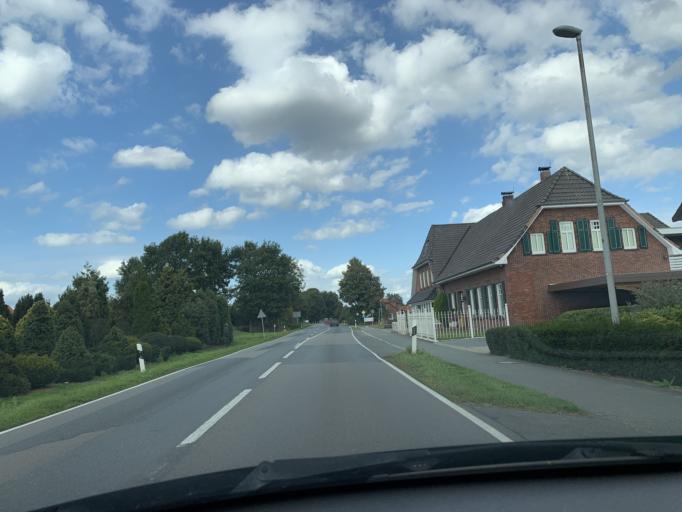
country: DE
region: Lower Saxony
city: Bad Zwischenahn
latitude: 53.1599
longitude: 7.9959
